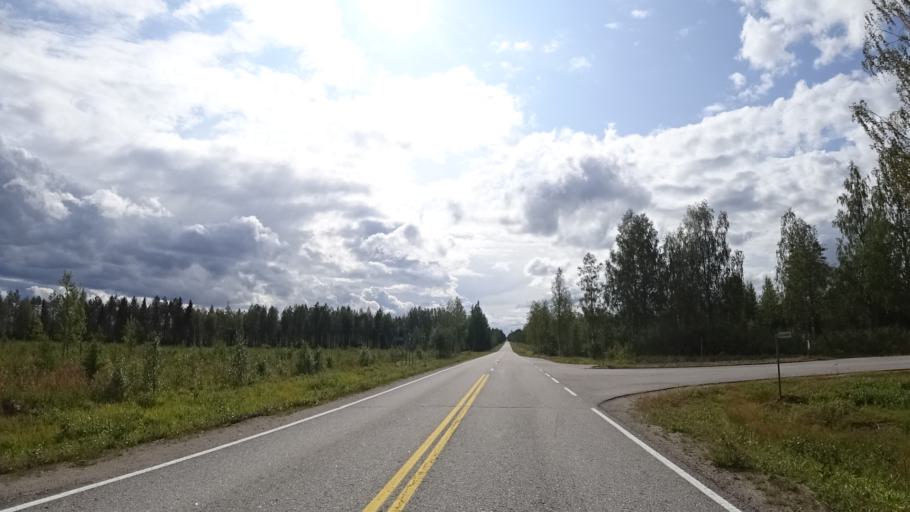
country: FI
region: North Karelia
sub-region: Joensuu
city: Ilomantsi
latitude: 62.7666
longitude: 31.0330
